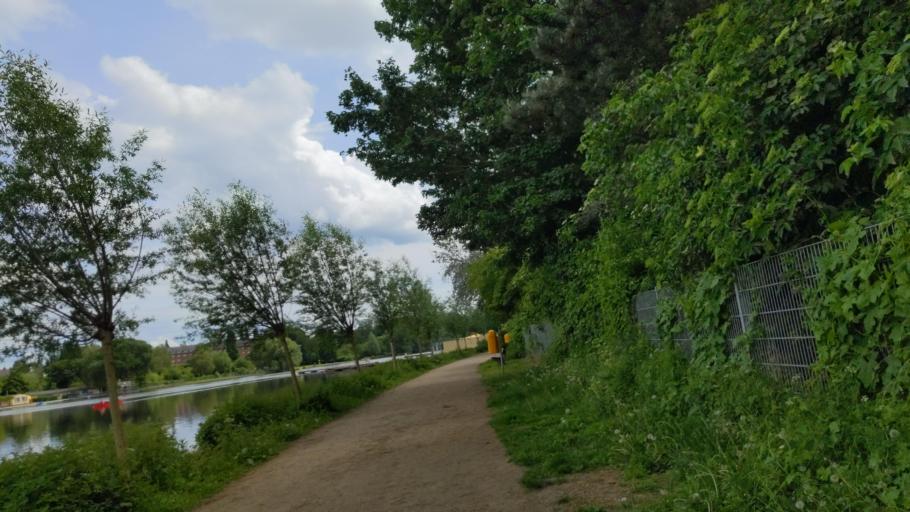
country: DE
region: Schleswig-Holstein
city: Luebeck
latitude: 53.8709
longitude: 10.7032
